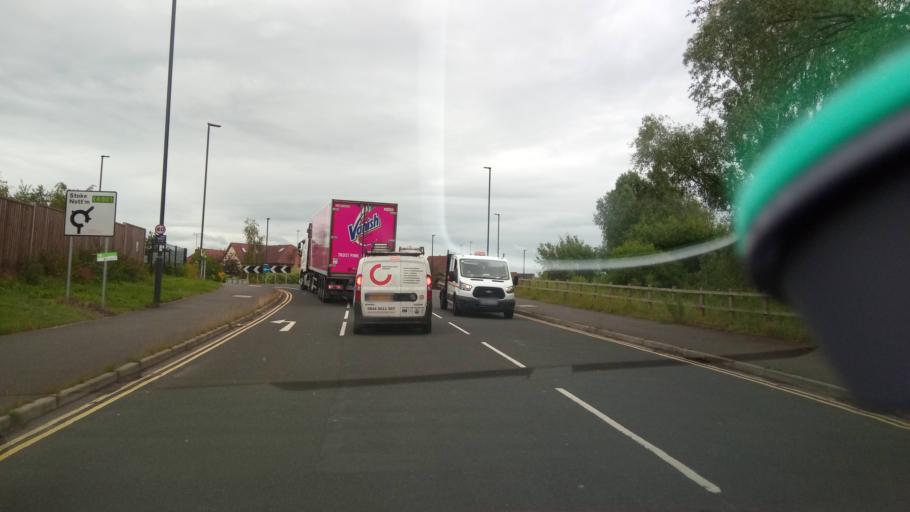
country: GB
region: England
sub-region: Derbyshire
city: Melbourne
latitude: 52.8672
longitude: -1.4500
